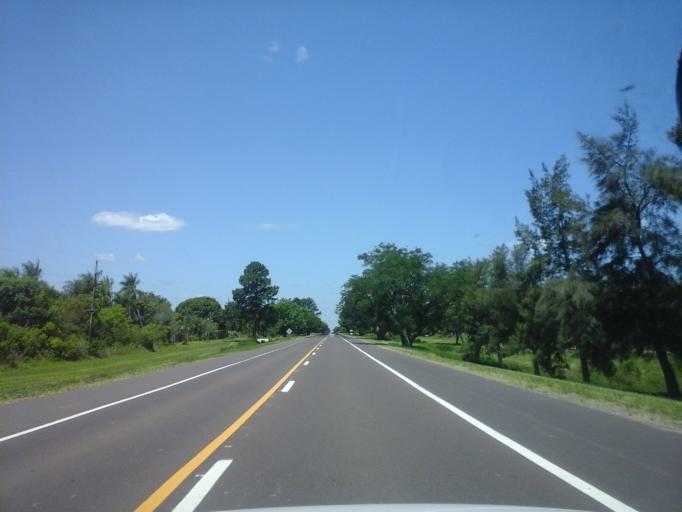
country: AR
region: Corrientes
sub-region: Departamento de San Cosme
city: San Cosme
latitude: -27.3681
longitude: -58.4055
